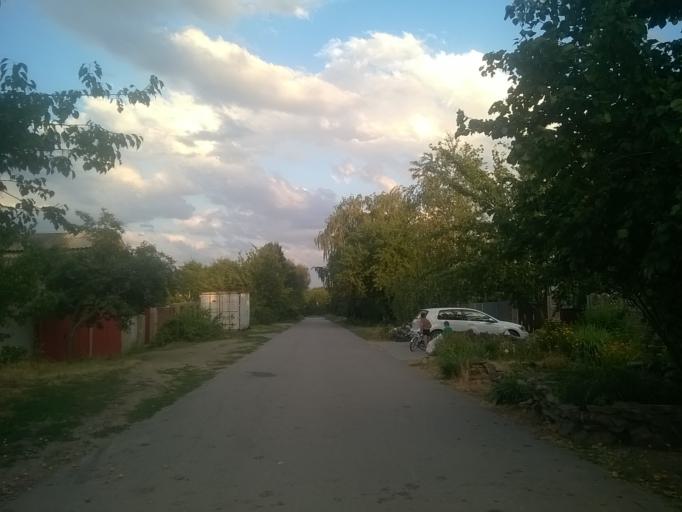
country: RU
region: Rostov
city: Donetsk
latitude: 48.3339
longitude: 39.9583
